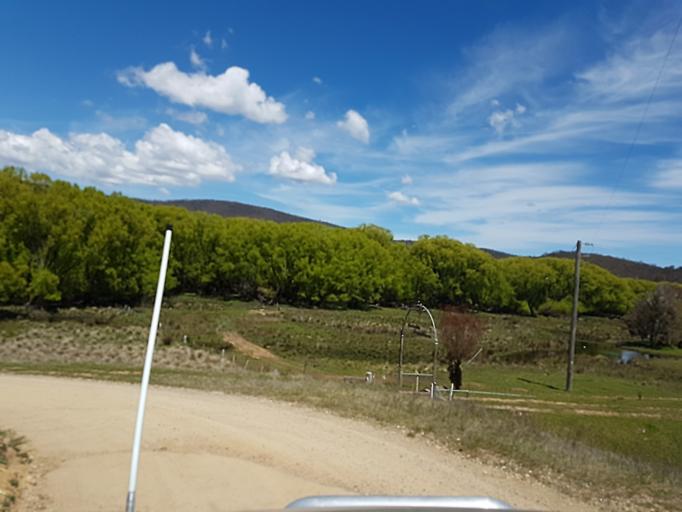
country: AU
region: Victoria
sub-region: Alpine
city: Mount Beauty
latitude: -37.0916
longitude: 147.4030
